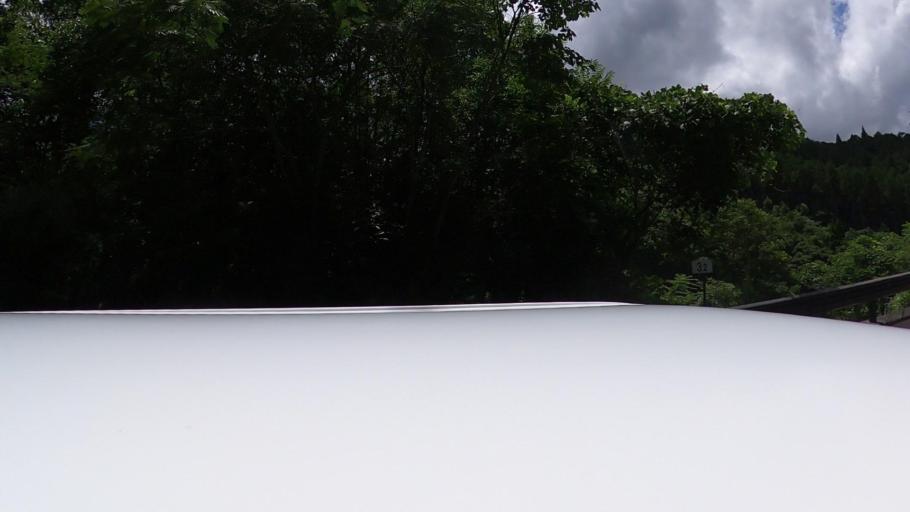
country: JP
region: Miyazaki
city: Nobeoka
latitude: 32.5770
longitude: 131.5240
